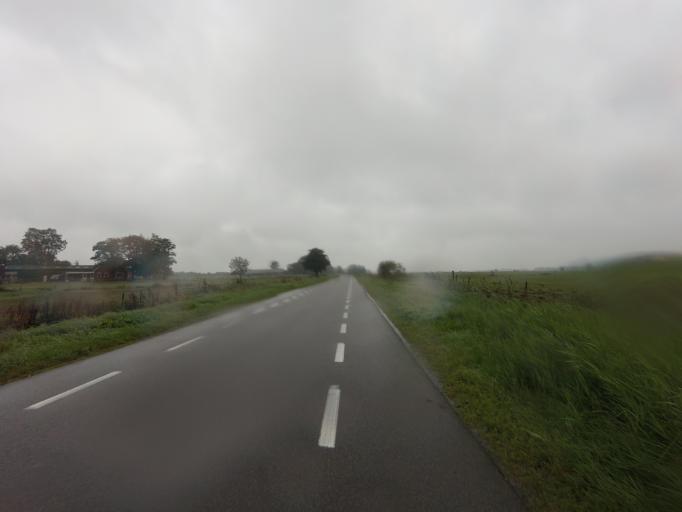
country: NL
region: Friesland
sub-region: Gemeente Smallingerland
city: Oudega
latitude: 53.0966
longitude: 5.9601
